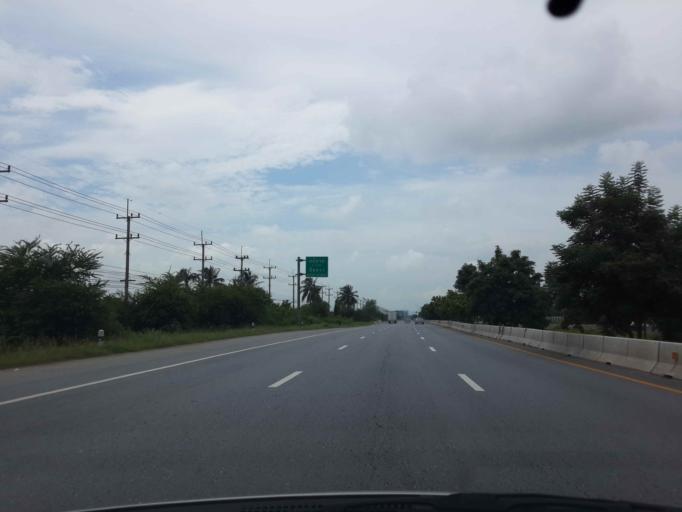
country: TH
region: Ratchaburi
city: Pak Tho
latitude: 13.3456
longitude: 99.8829
